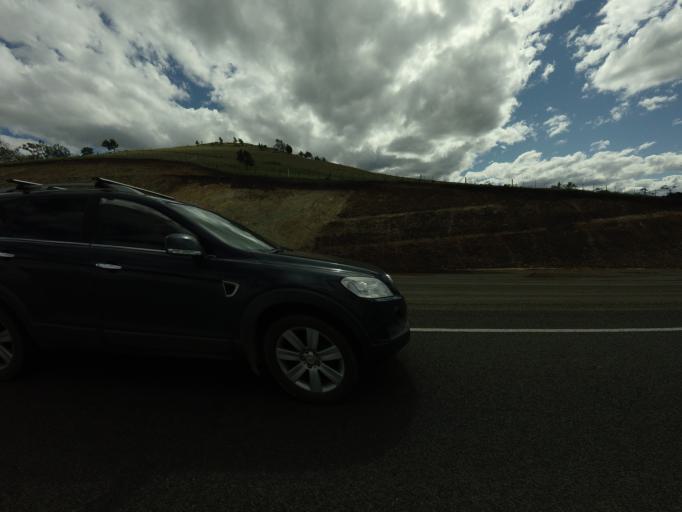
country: AU
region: Tasmania
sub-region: Brighton
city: Bridgewater
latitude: -42.2208
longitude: 147.4106
